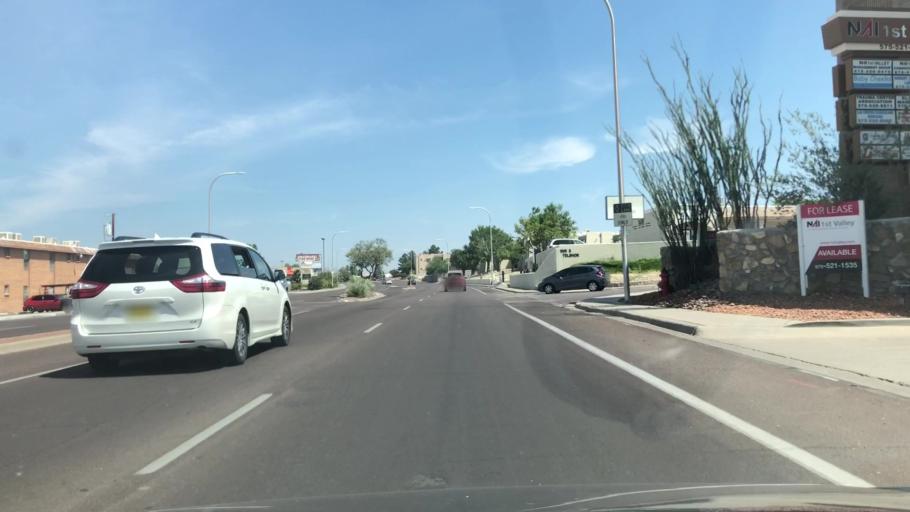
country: US
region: New Mexico
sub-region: Dona Ana County
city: University Park
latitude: 32.3056
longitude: -106.7383
